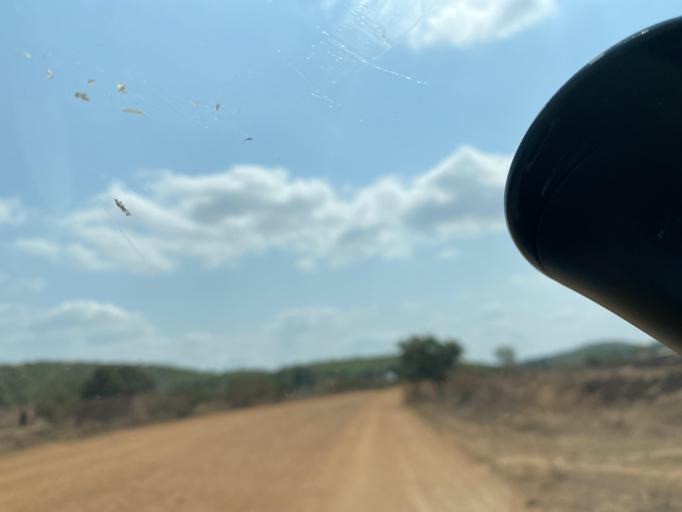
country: ZM
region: Lusaka
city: Chongwe
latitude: -15.6031
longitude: 28.7480
